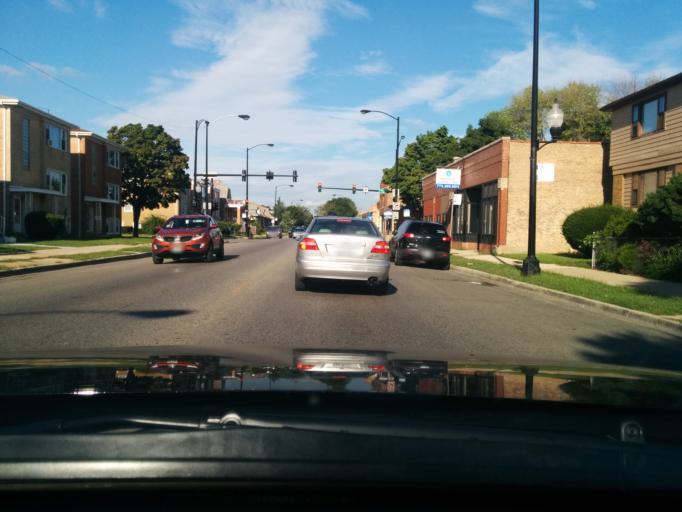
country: US
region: Illinois
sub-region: Cook County
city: Harwood Heights
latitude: 41.9459
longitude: -87.7708
